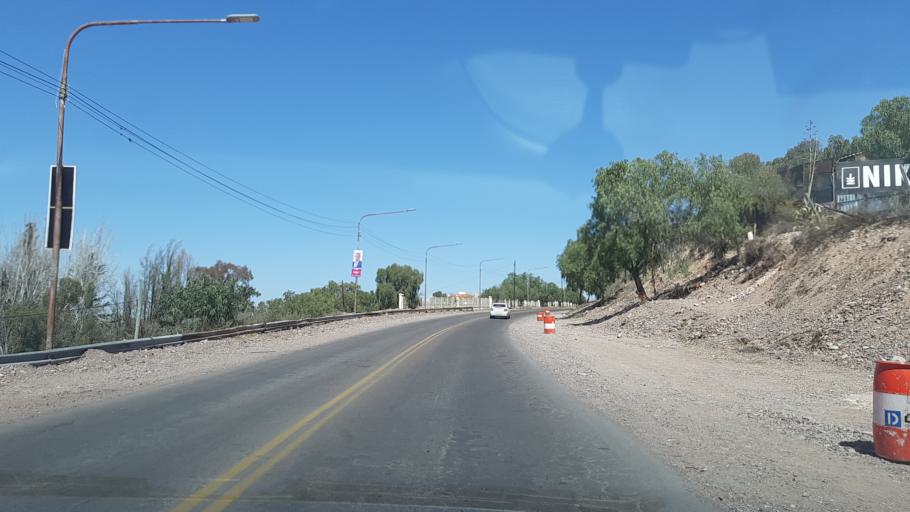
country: AR
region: Mendoza
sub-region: Departamento de Godoy Cruz
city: Godoy Cruz
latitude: -32.9645
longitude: -68.8719
